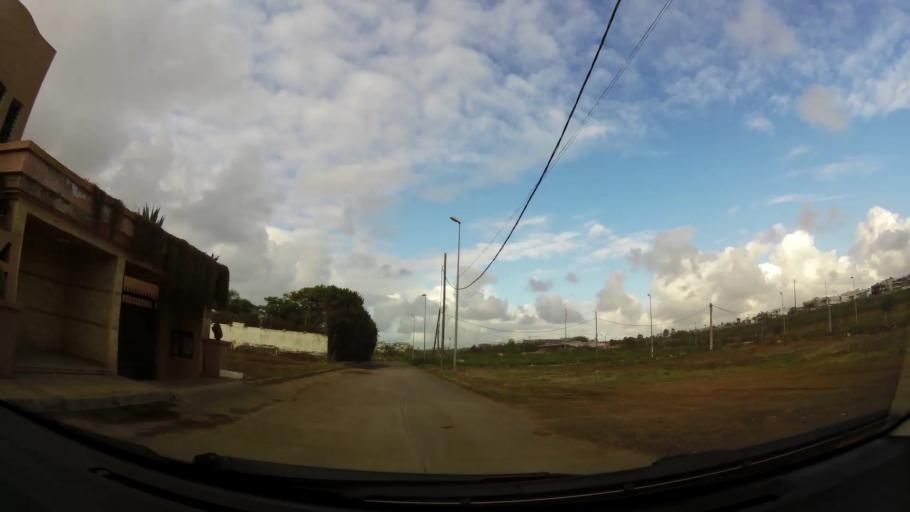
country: MA
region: Grand Casablanca
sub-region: Casablanca
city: Casablanca
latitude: 33.5765
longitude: -7.6931
